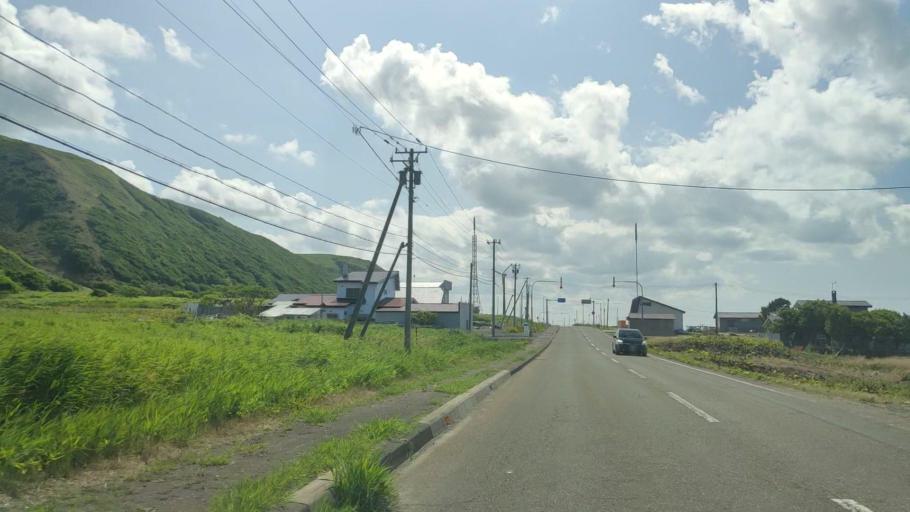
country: JP
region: Hokkaido
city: Wakkanai
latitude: 45.4105
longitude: 141.6359
